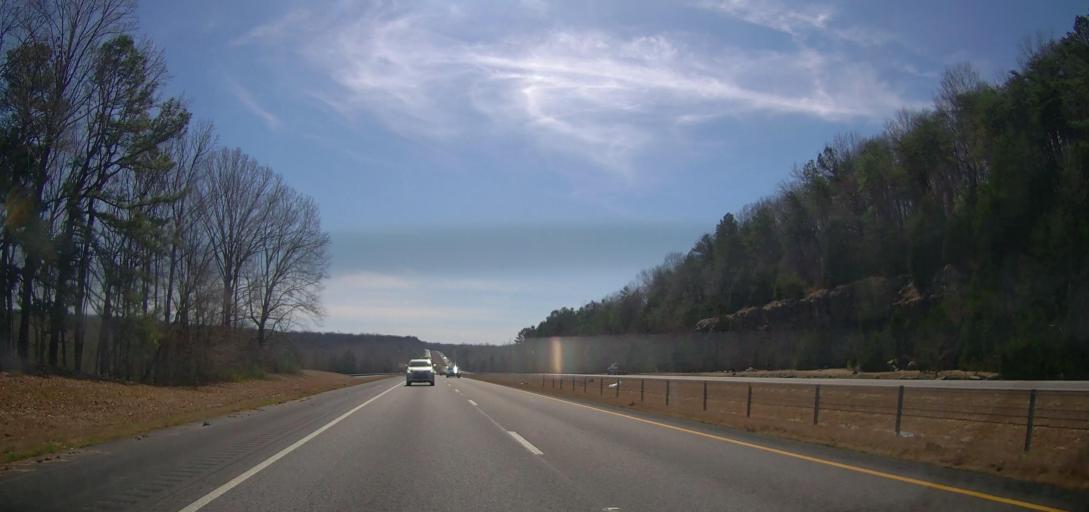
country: US
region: Alabama
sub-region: Morgan County
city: Falkville
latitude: 34.3144
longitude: -86.9017
